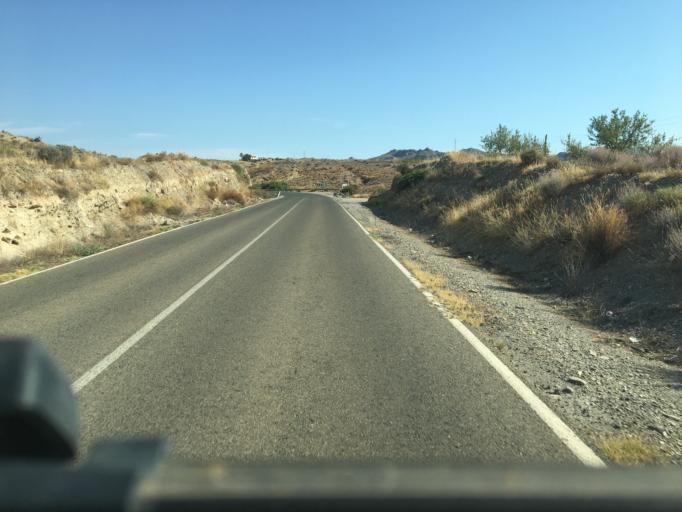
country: ES
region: Andalusia
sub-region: Provincia de Almeria
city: Huercal-Overa
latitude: 37.4271
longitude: -1.9713
